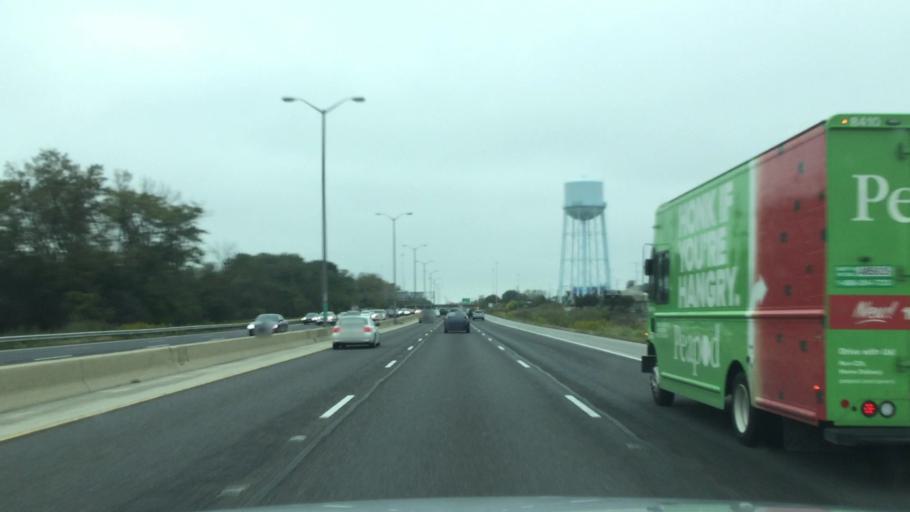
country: US
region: Illinois
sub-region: Cook County
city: Northfield
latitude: 42.1227
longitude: -87.7817
